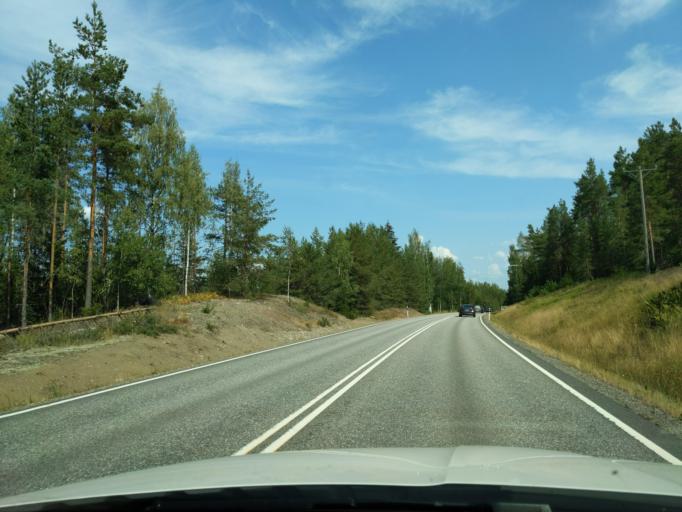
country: FI
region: Paijanne Tavastia
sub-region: Lahti
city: Padasjoki
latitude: 61.3363
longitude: 25.2244
